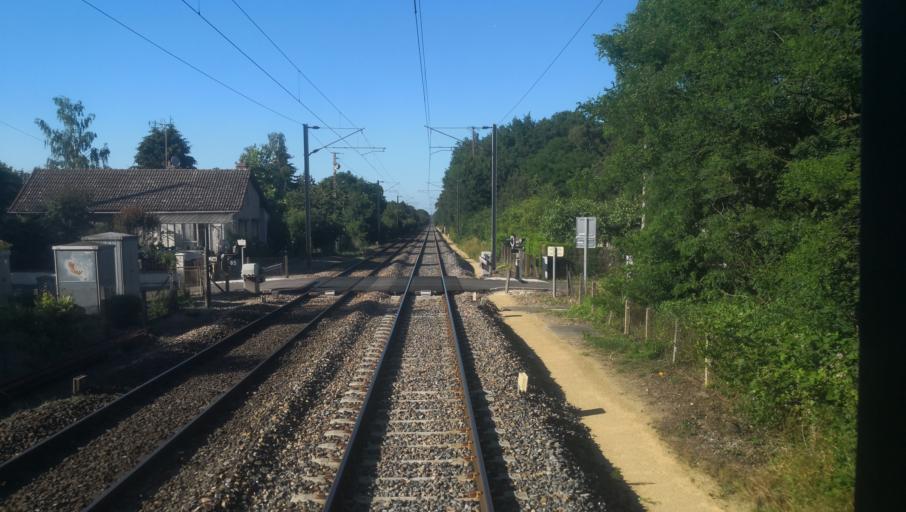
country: FR
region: Bourgogne
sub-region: Departement de la Nievre
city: Cosne-Cours-sur-Loire
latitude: 47.3618
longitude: 2.8927
